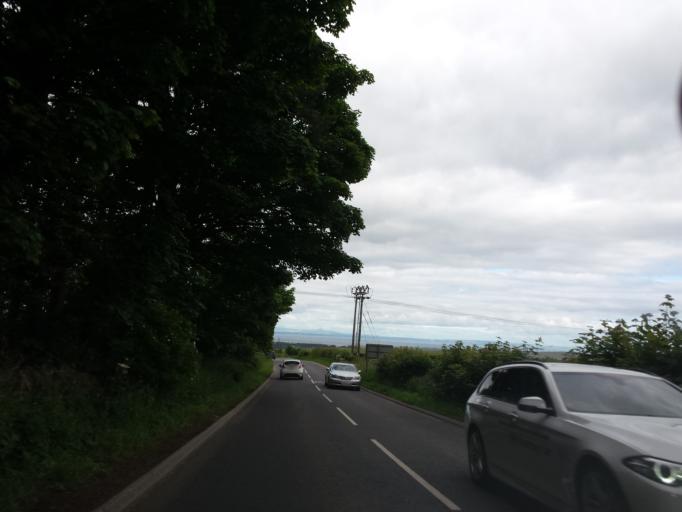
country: GB
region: Scotland
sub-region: East Lothian
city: Haddington
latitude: 55.9766
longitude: -2.8077
